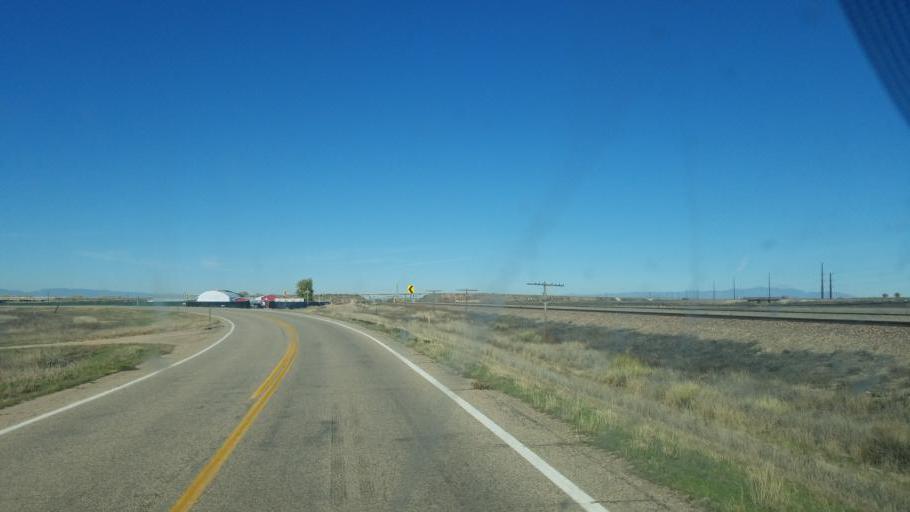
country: US
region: Colorado
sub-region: Pueblo County
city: Pueblo
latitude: 38.2642
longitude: -104.3607
